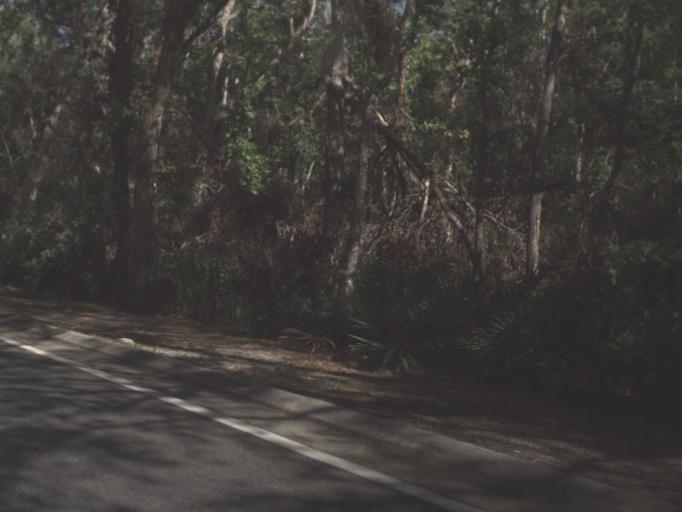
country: US
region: Florida
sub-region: Flagler County
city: Palm Coast
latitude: 29.5567
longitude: -81.1983
